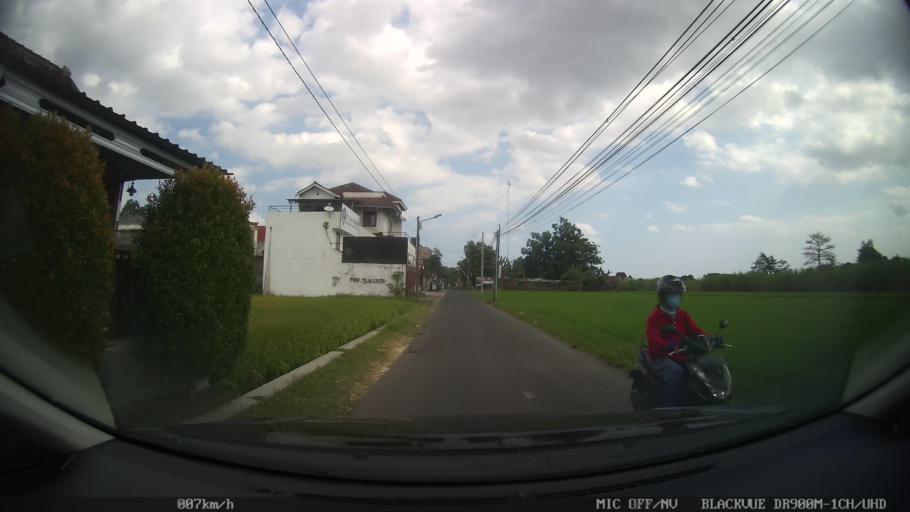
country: ID
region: Daerah Istimewa Yogyakarta
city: Gamping Lor
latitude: -7.7743
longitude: 110.3373
